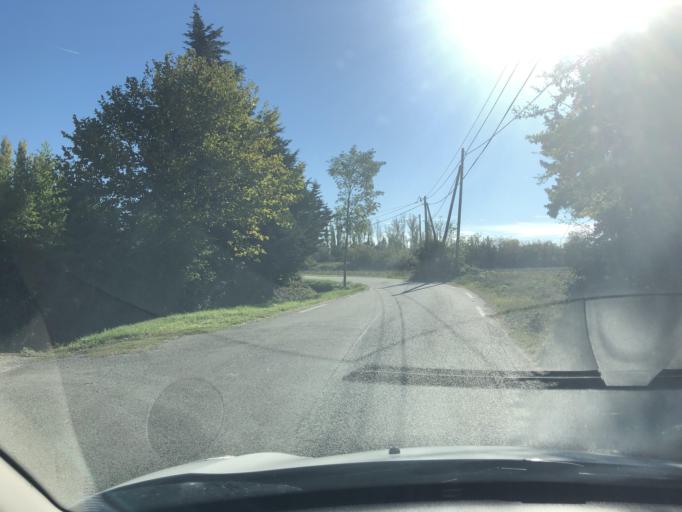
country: FR
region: Provence-Alpes-Cote d'Azur
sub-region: Departement du Vaucluse
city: Entraigues-sur-la-Sorgue
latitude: 43.9919
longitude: 4.9361
